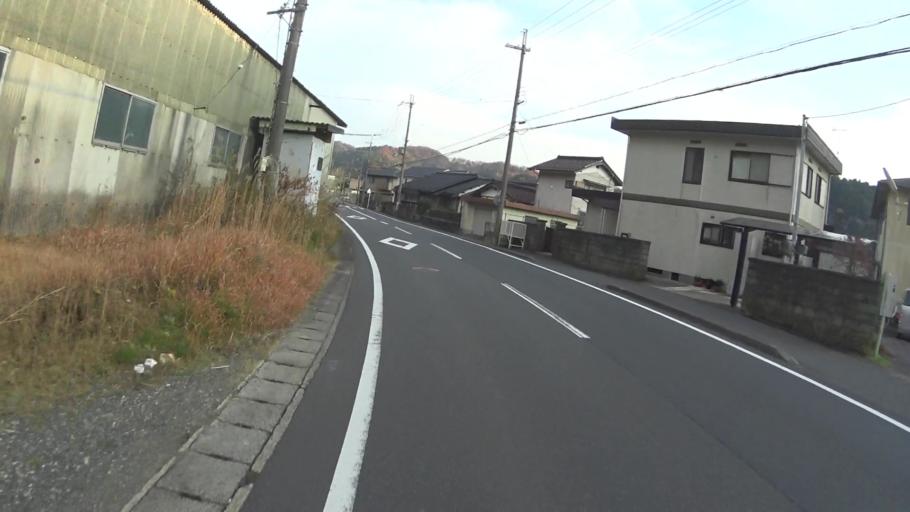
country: JP
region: Kyoto
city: Maizuru
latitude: 35.4993
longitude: 135.4331
